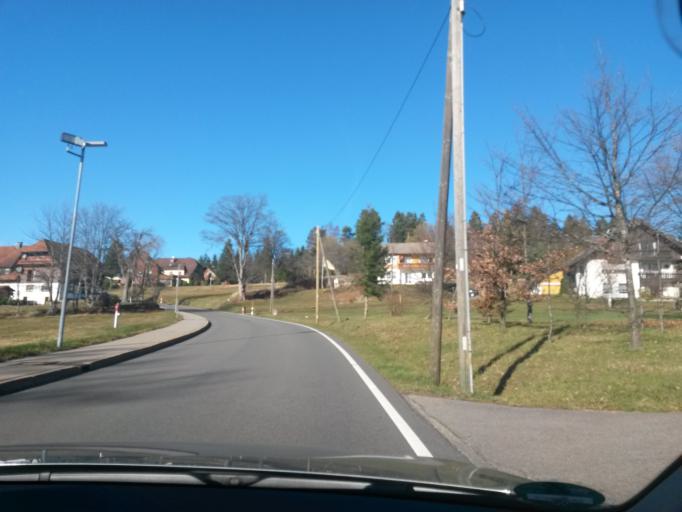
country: DE
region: Baden-Wuerttemberg
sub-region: Karlsruhe Region
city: Bad Rippoldsau-Schapbach
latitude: 48.4661
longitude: 8.2986
